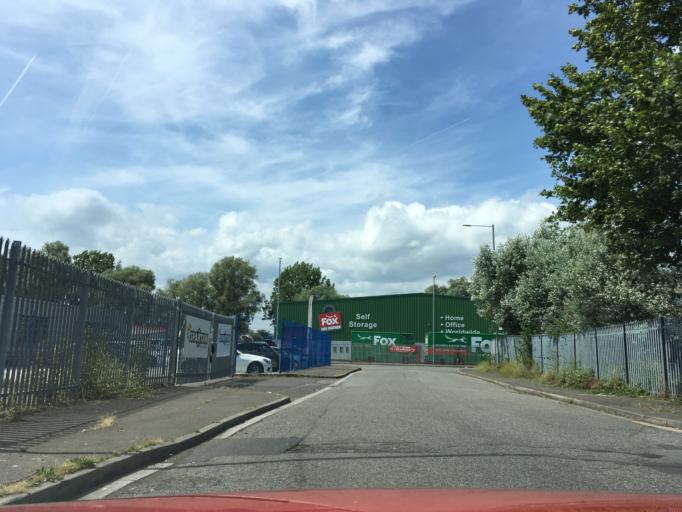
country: GB
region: Wales
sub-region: Newport
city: Nash
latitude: 51.5703
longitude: -2.9473
